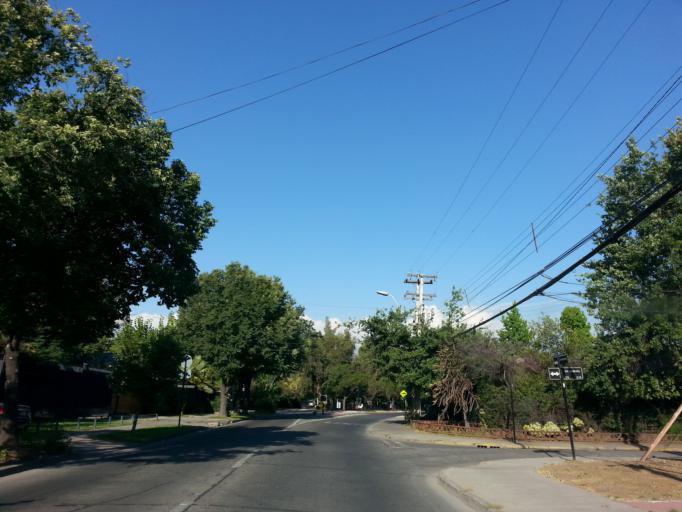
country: CL
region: Santiago Metropolitan
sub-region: Provincia de Santiago
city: Villa Presidente Frei, Nunoa, Santiago, Chile
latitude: -33.3855
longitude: -70.5480
